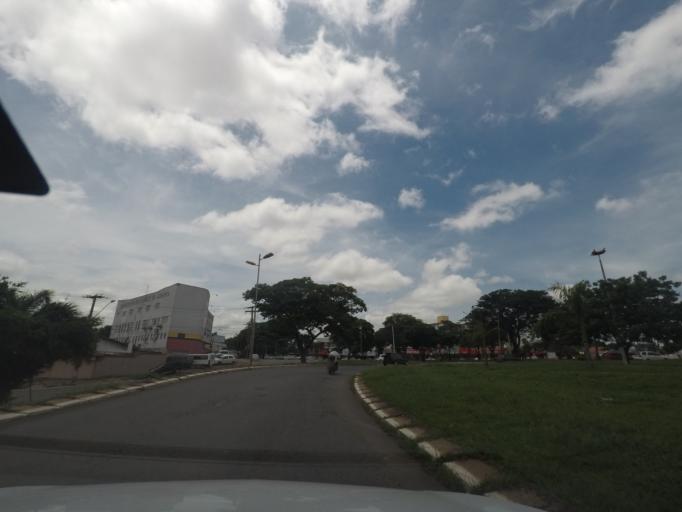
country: BR
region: Goias
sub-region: Goiania
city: Goiania
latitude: -16.6707
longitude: -49.2349
